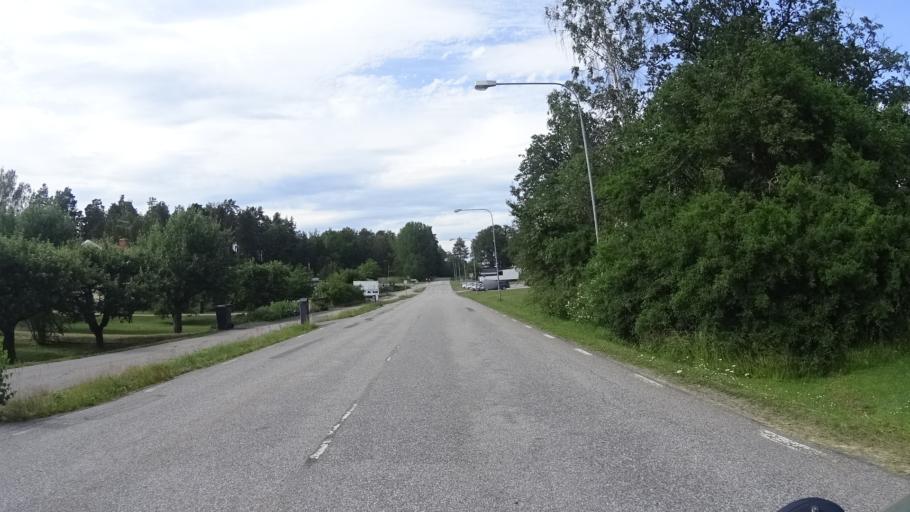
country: SE
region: Kalmar
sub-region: Vasterviks Kommun
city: Gamleby
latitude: 57.9060
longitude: 16.4117
